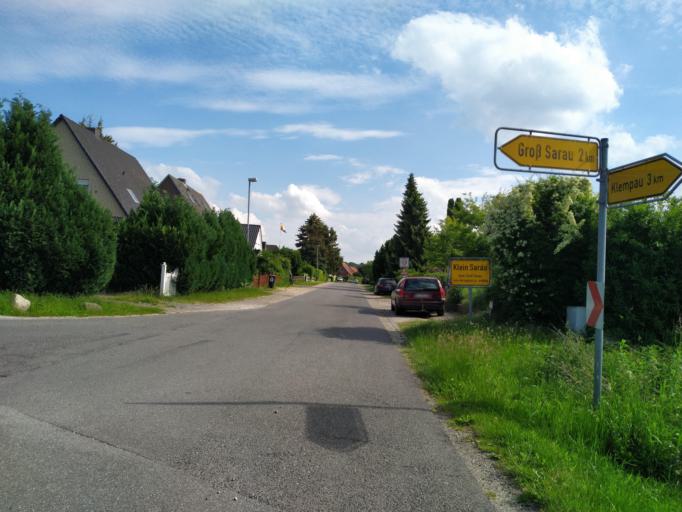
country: DE
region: Schleswig-Holstein
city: Gross Sarau
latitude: 53.7711
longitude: 10.7073
